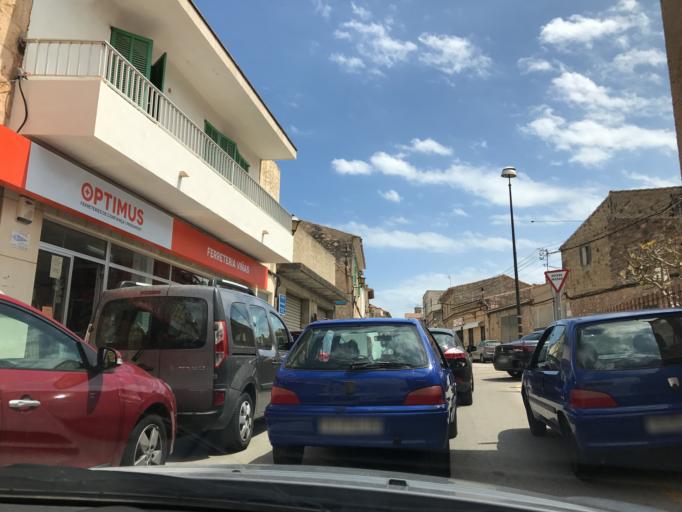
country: ES
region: Balearic Islands
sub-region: Illes Balears
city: Son Servera
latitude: 39.6240
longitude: 3.3572
